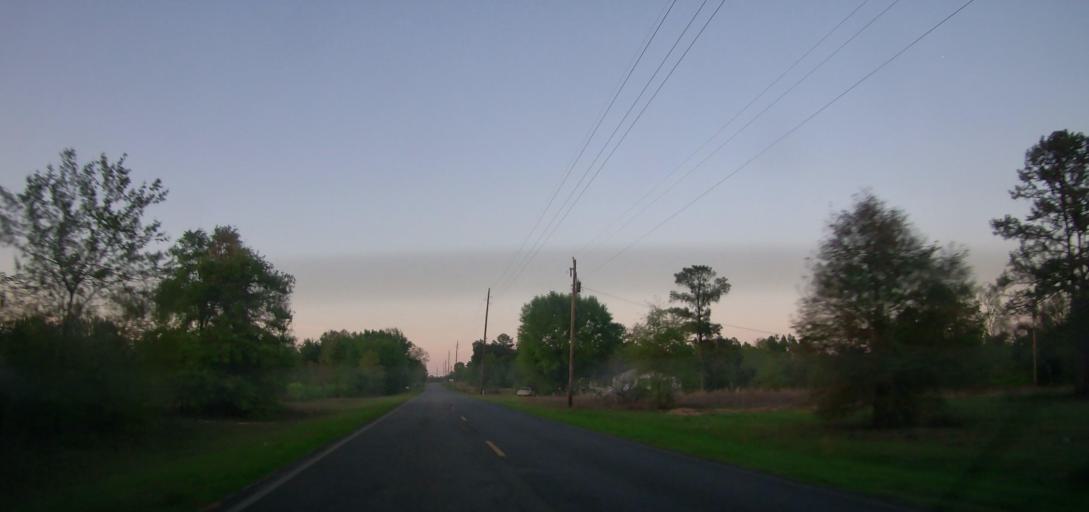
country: US
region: Georgia
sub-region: Marion County
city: Buena Vista
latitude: 32.2703
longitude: -84.5498
